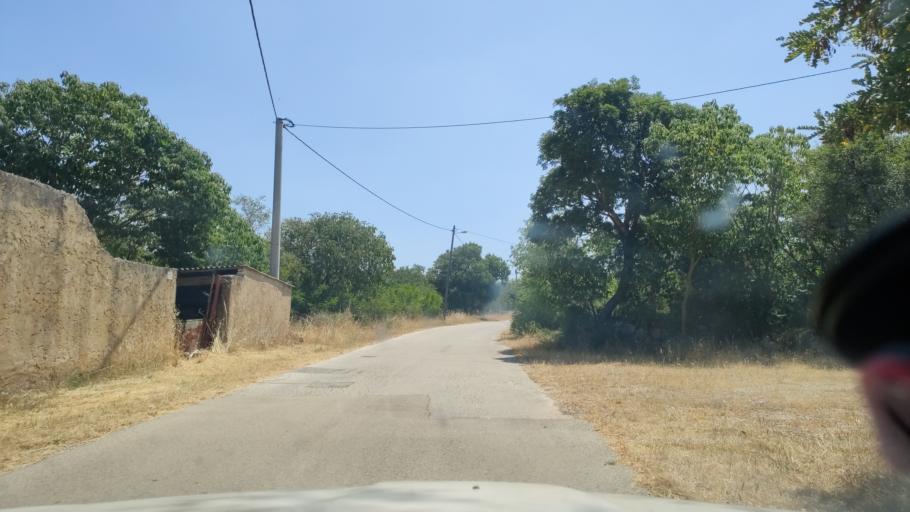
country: HR
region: Sibensko-Kniniska
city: Kistanje
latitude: 43.9566
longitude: 15.8779
